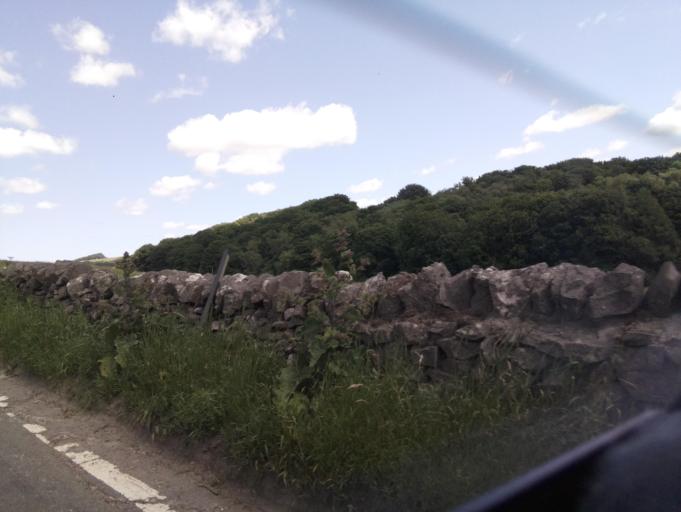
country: GB
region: England
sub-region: Derbyshire
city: Ashbourne
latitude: 53.0964
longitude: -1.7731
